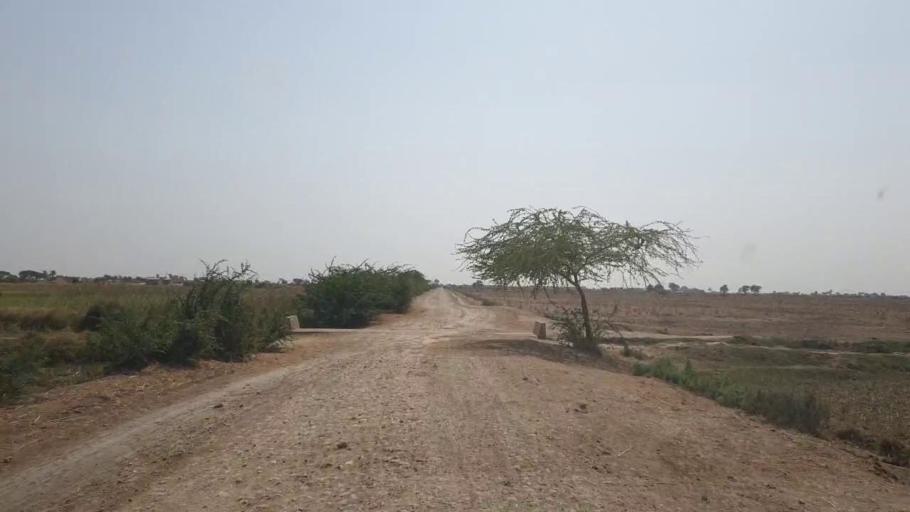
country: PK
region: Sindh
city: Jati
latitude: 24.4312
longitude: 68.5524
